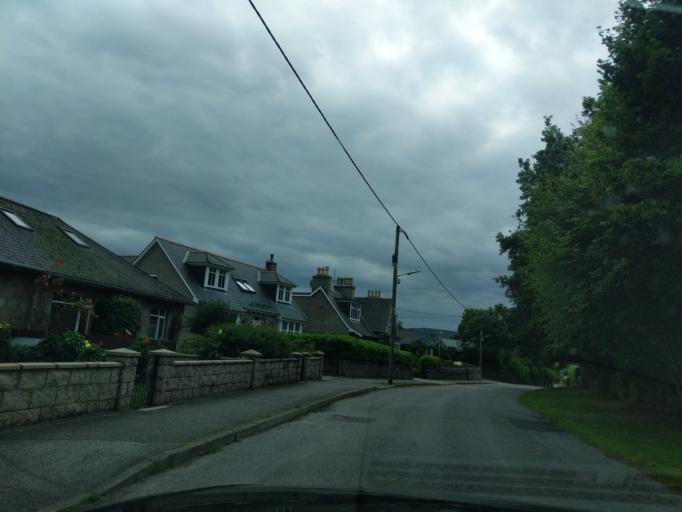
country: GB
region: Scotland
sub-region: Aberdeenshire
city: Aboyne
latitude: 57.0790
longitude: -2.7727
